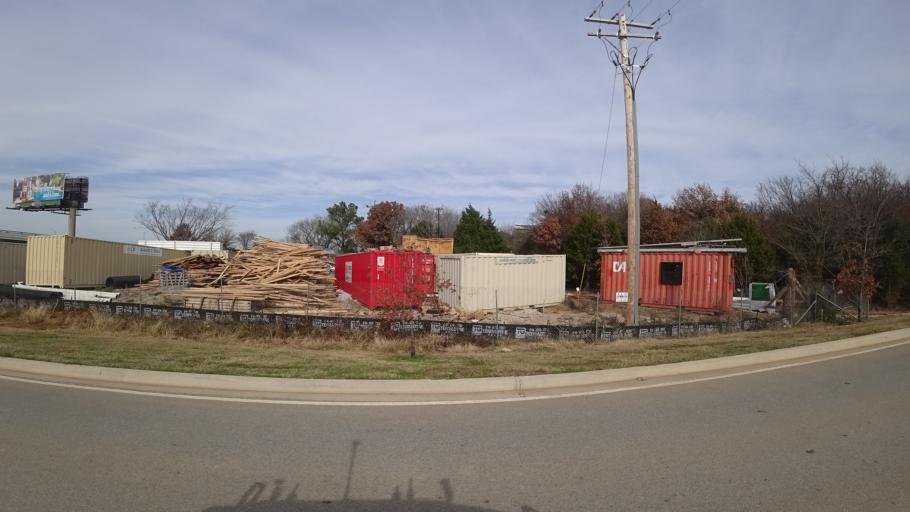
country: US
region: Texas
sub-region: Denton County
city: Highland Village
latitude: 33.0850
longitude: -97.0257
